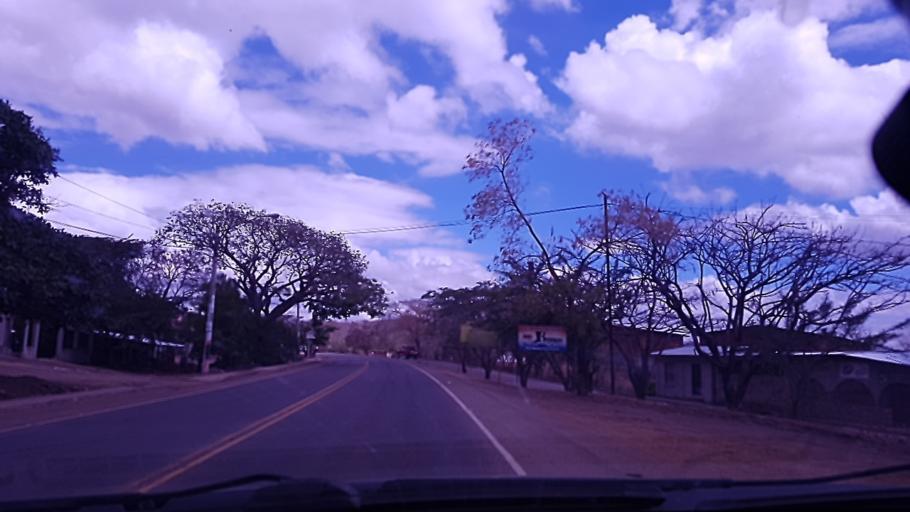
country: NI
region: Esteli
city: Condega
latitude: 13.3676
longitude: -86.3986
